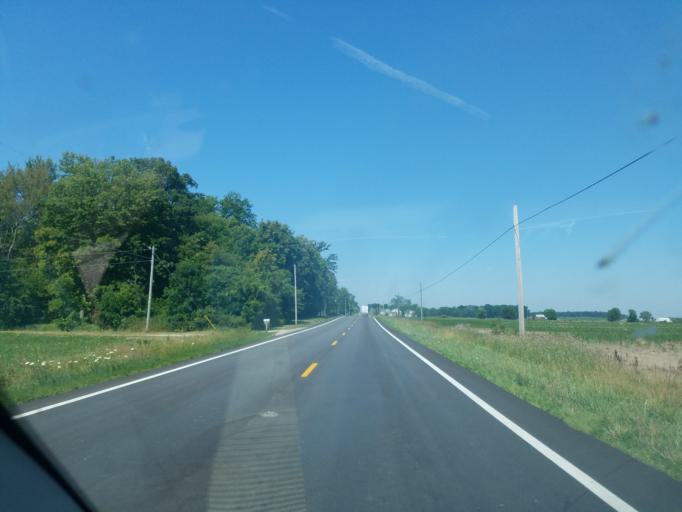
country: US
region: Ohio
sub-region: Shelby County
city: Jackson Center
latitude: 40.4396
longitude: -84.0826
